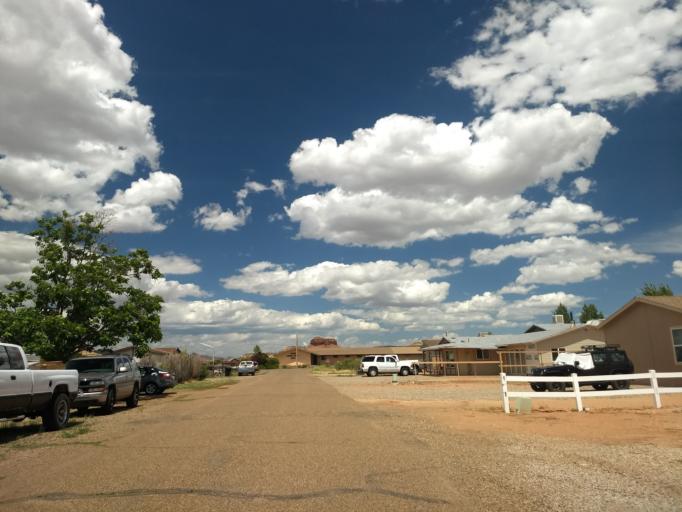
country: US
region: Arizona
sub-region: Coconino County
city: Fredonia
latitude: 36.9605
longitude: -112.5256
